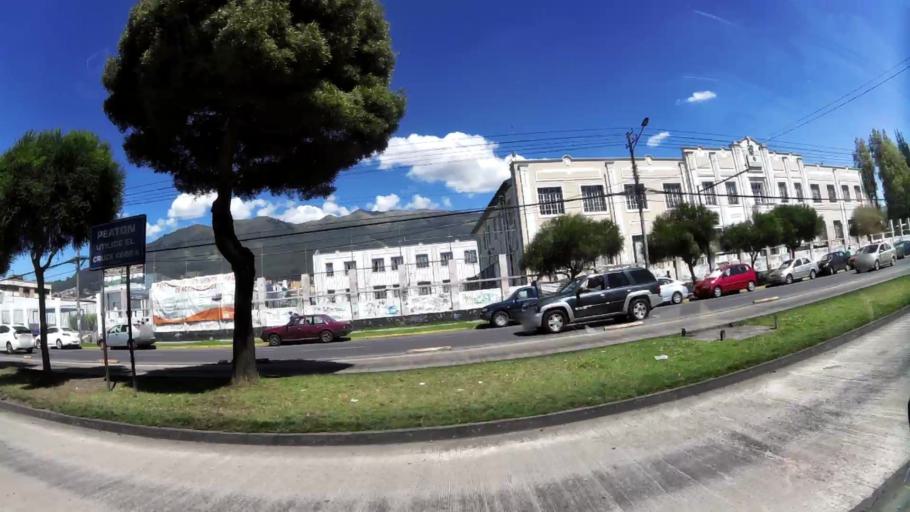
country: EC
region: Pichincha
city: Quito
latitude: -0.1373
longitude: -78.4932
